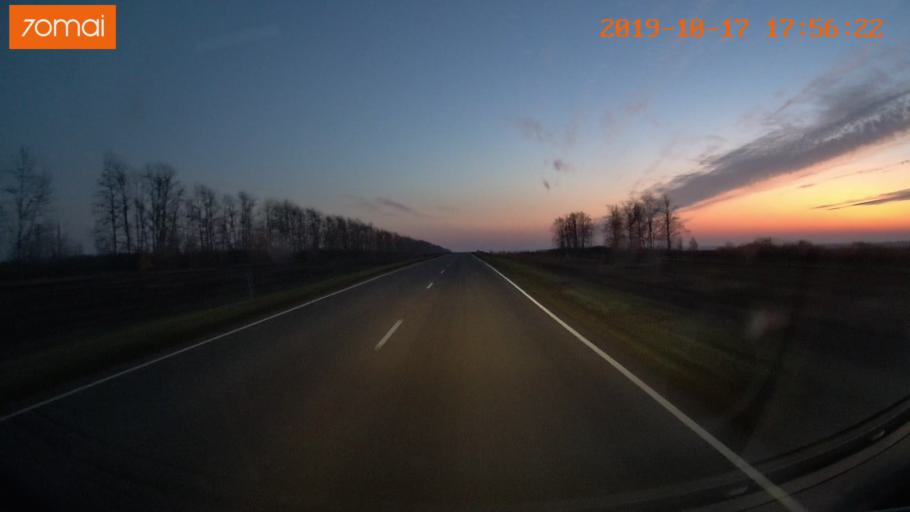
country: RU
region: Tula
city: Kurkino
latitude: 53.5801
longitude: 38.6473
